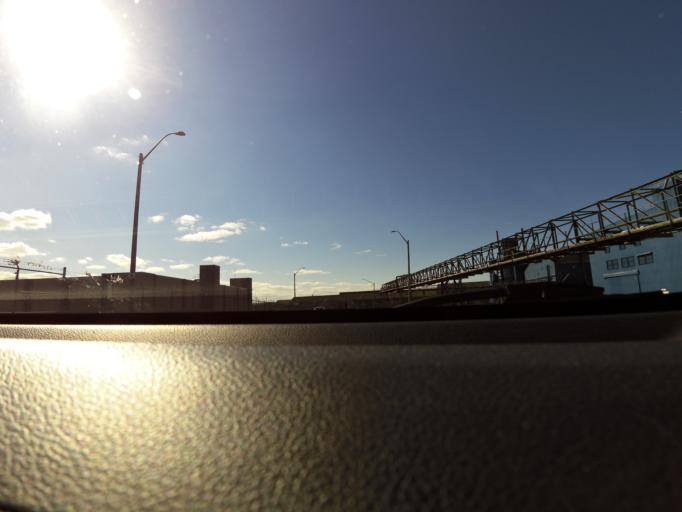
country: CA
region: Ontario
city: Hamilton
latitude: 43.2648
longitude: -79.8223
